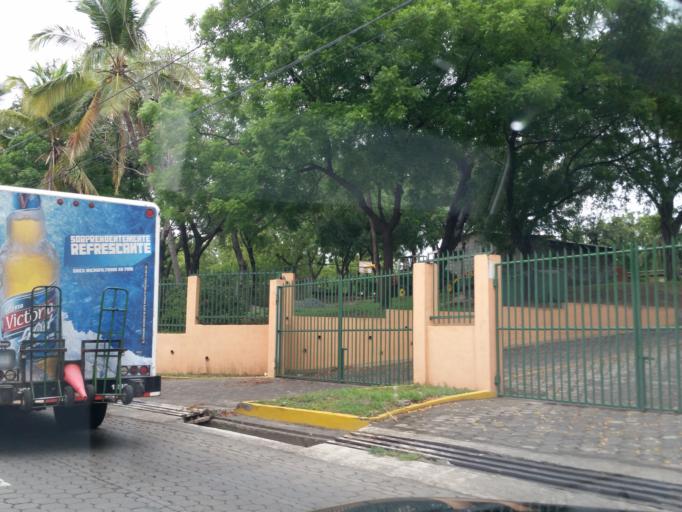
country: NI
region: Managua
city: Managua
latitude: 12.1123
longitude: -86.2685
